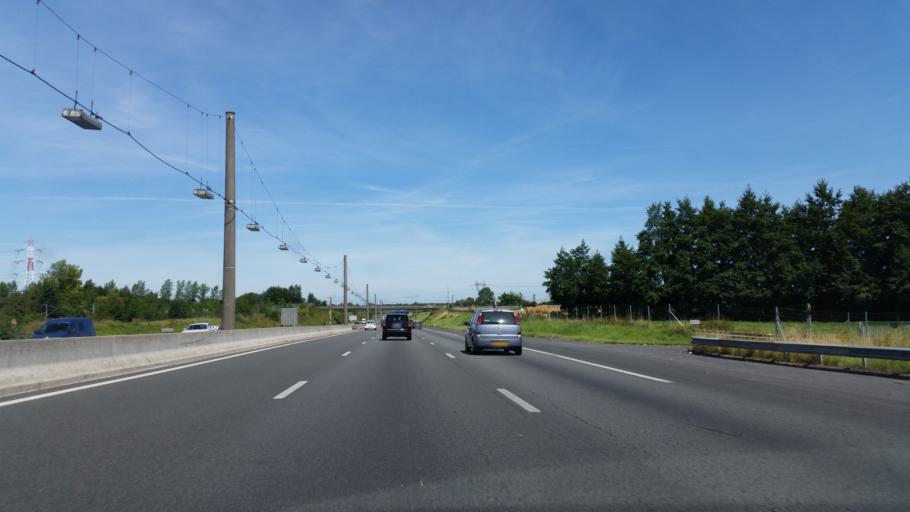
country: FR
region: Nord-Pas-de-Calais
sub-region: Departement du Pas-de-Calais
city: Fampoux
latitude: 50.2963
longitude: 2.8855
